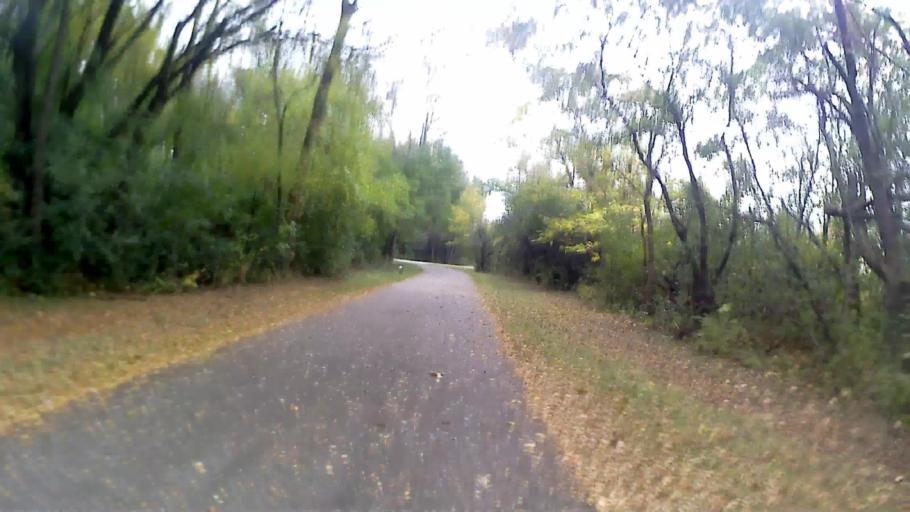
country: US
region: Illinois
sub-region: Kane County
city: Montgomery
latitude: 41.7587
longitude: -88.3858
